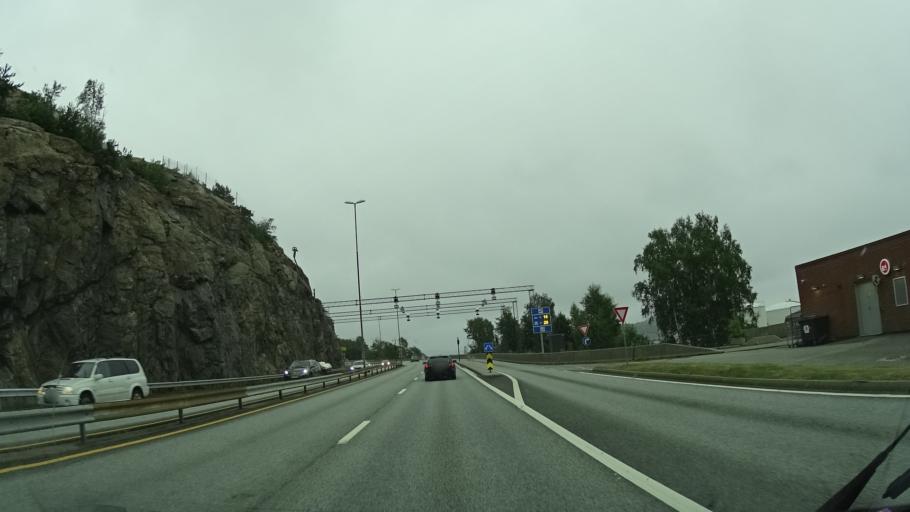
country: NO
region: Vest-Agder
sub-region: Kristiansand
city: Kristiansand
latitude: 58.1412
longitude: 7.9753
